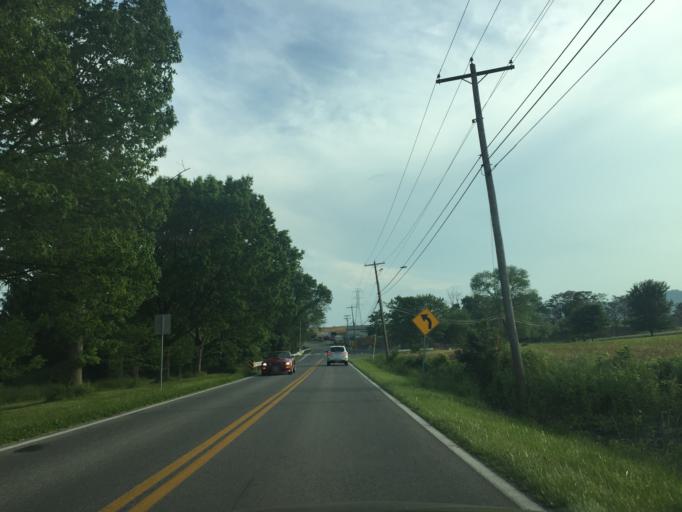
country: US
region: Maryland
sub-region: Frederick County
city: Adamstown
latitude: 39.3310
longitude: -77.4873
